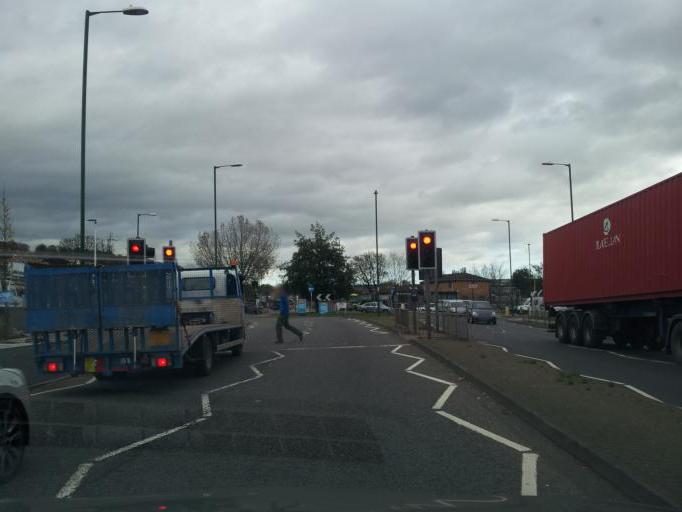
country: GB
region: England
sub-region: Nottinghamshire
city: West Bridgford
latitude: 52.9466
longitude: -1.1242
